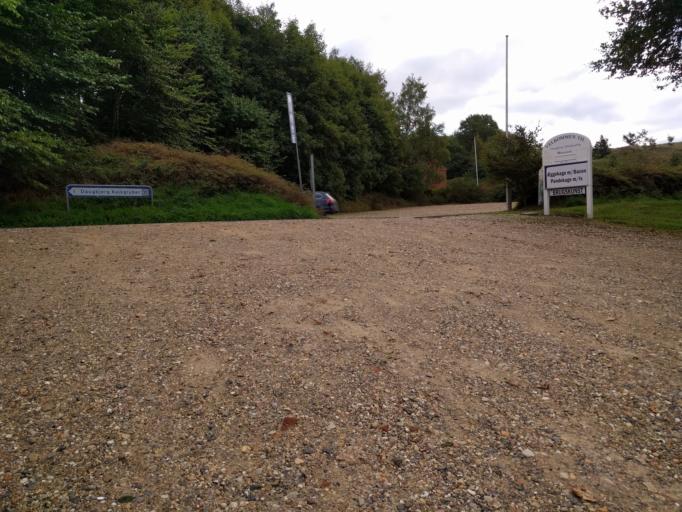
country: DK
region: Central Jutland
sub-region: Viborg Kommune
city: Stoholm
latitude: 56.4381
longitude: 9.1306
